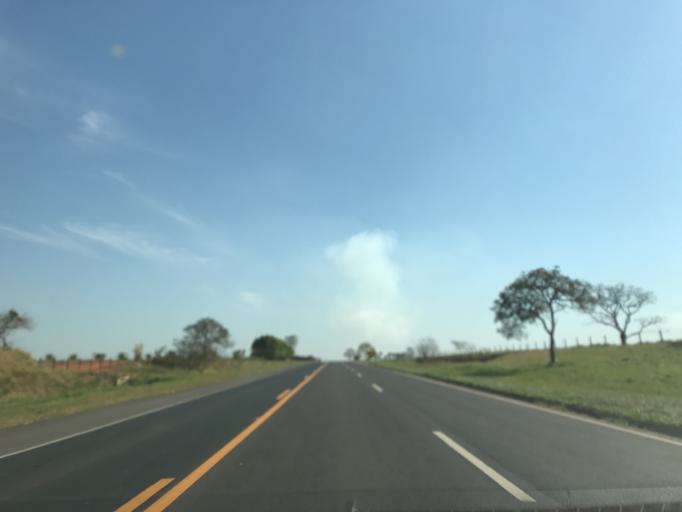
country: BR
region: Sao Paulo
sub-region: Penapolis
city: Penapolis
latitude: -21.3538
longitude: -50.0605
